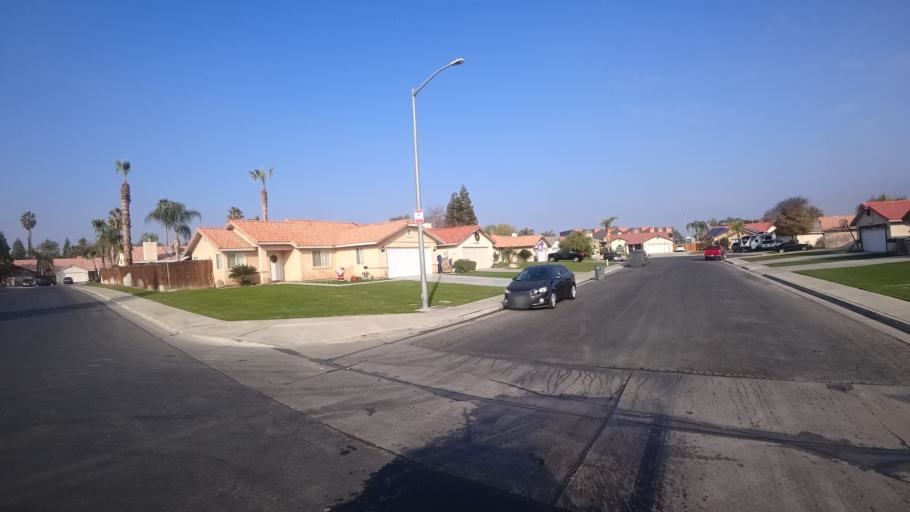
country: US
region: California
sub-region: Kern County
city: Greenfield
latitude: 35.3059
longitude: -119.0696
